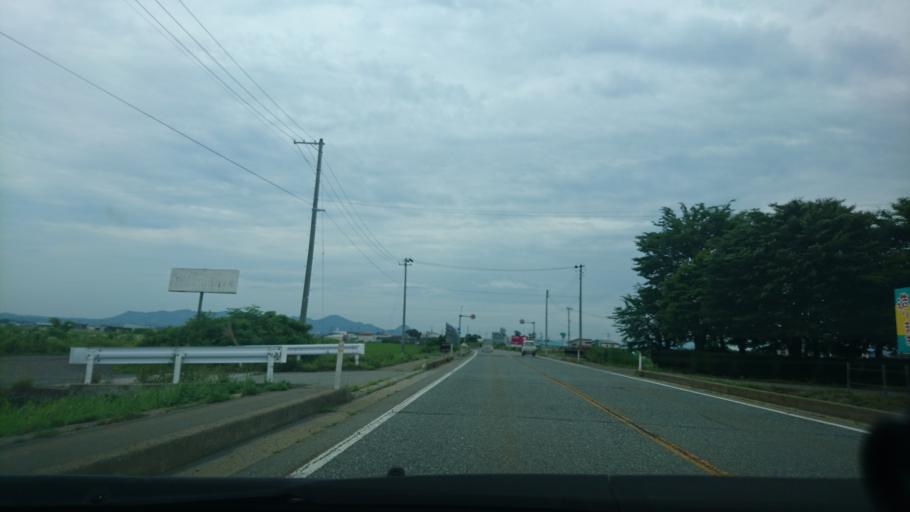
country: JP
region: Akita
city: Omagari
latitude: 39.4188
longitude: 140.5403
